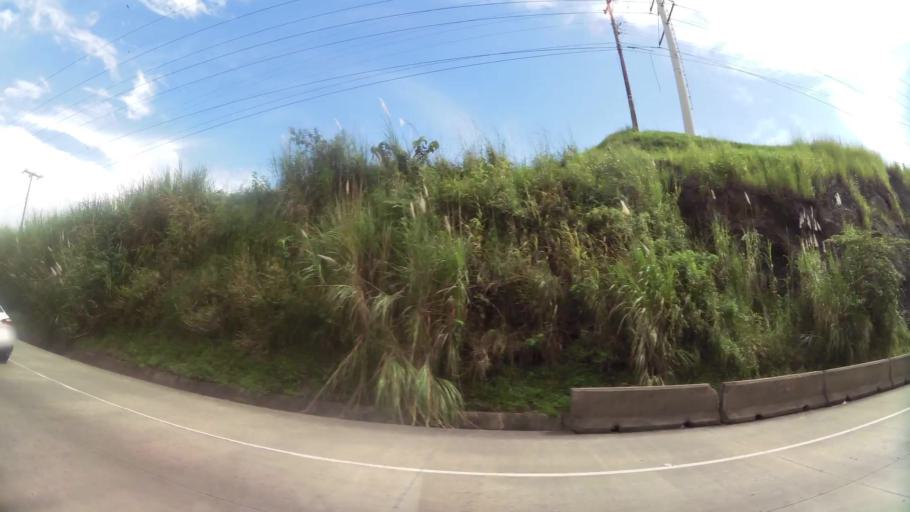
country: PA
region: Panama
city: Las Cumbres
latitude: 9.0554
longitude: -79.5159
